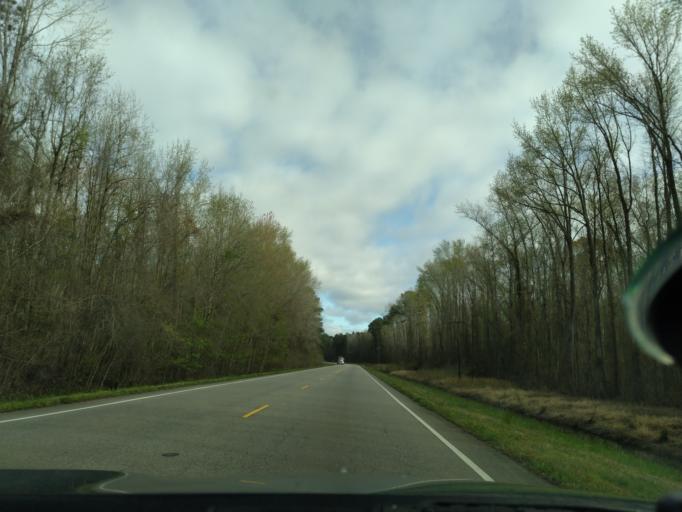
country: US
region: North Carolina
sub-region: Washington County
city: Plymouth
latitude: 35.8794
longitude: -76.6953
